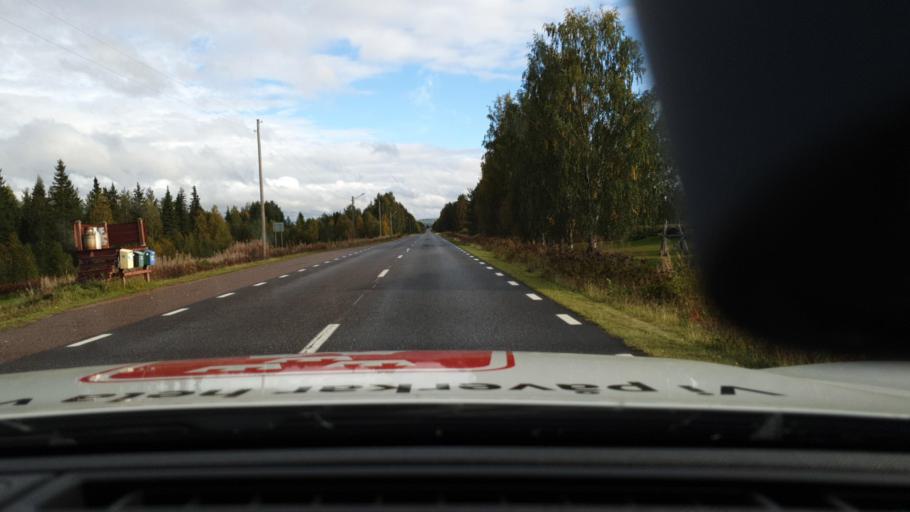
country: SE
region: Norrbotten
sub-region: Overkalix Kommun
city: OEverkalix
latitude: 66.9522
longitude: 22.7065
